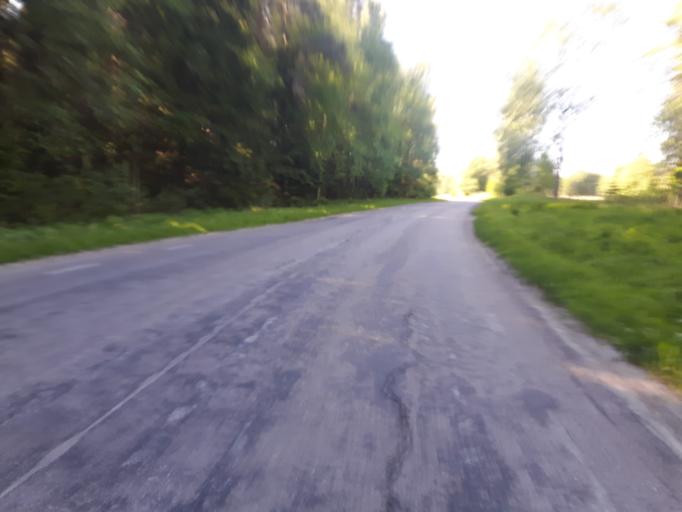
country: EE
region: Harju
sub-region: Loksa linn
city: Loksa
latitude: 59.5675
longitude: 25.9716
